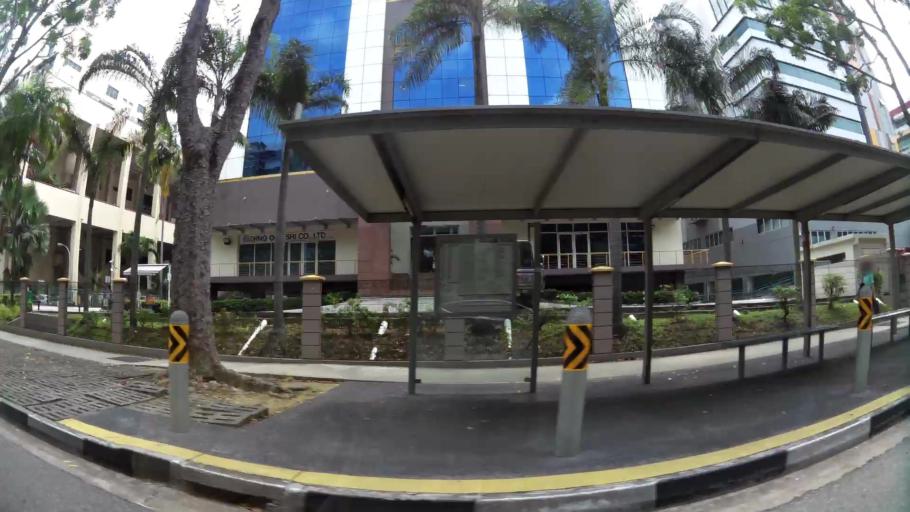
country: SG
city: Singapore
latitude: 1.3254
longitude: 103.8954
